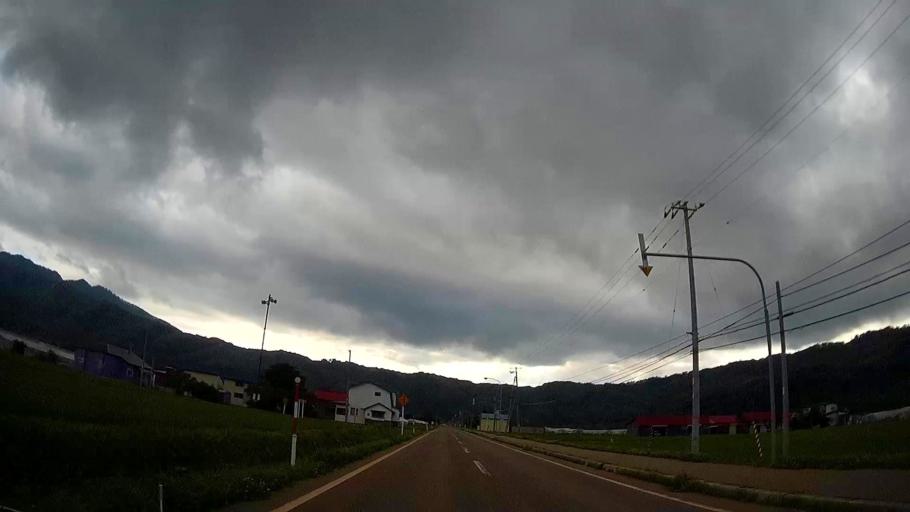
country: JP
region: Hokkaido
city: Nanae
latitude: 42.1211
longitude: 140.4396
